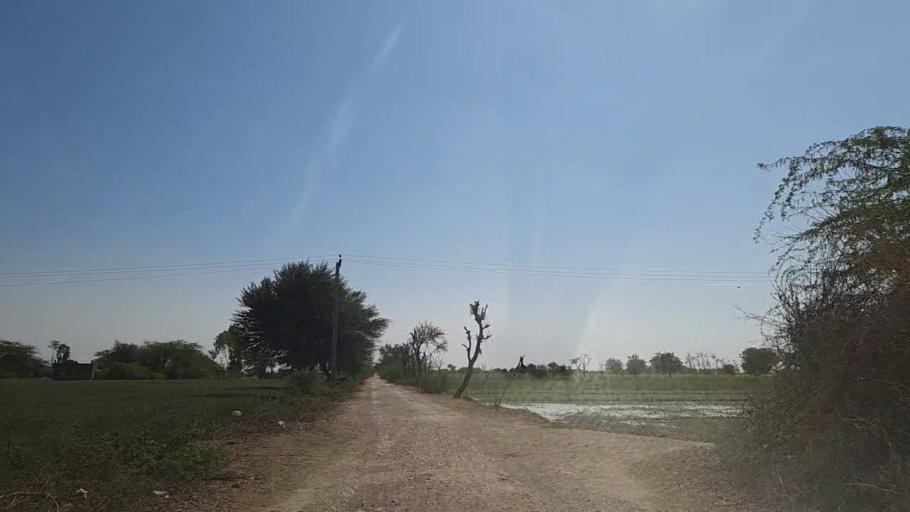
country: PK
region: Sindh
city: Kunri
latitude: 25.2806
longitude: 69.5226
